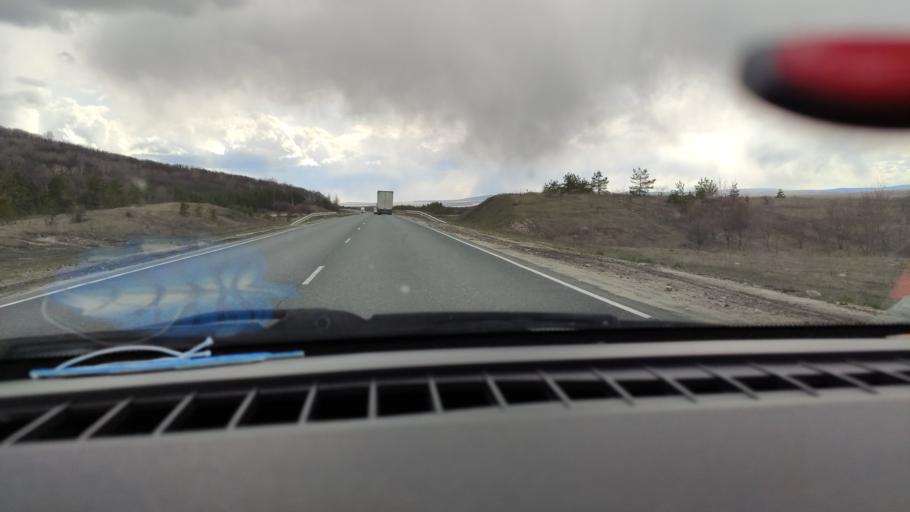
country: RU
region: Saratov
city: Alekseyevka
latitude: 52.3940
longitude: 47.9805
